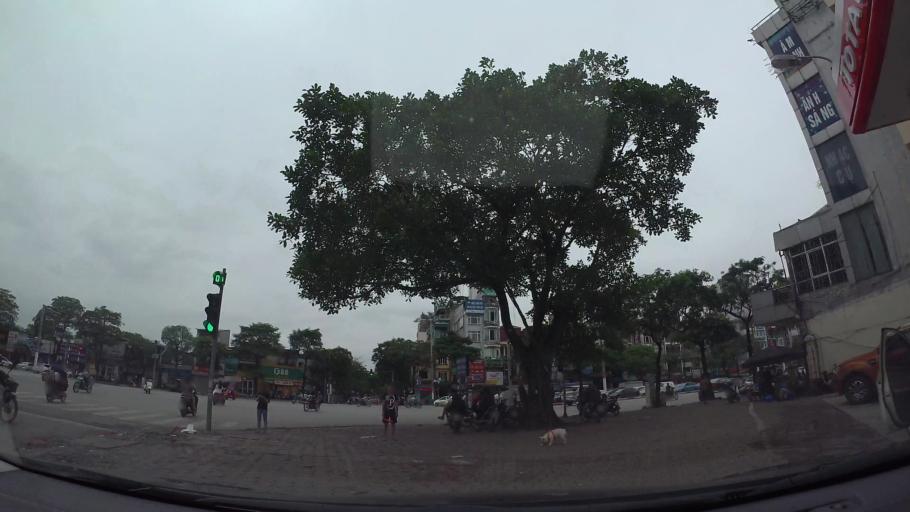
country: VN
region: Ha Noi
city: Hai BaTrung
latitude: 21.0093
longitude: 105.8545
